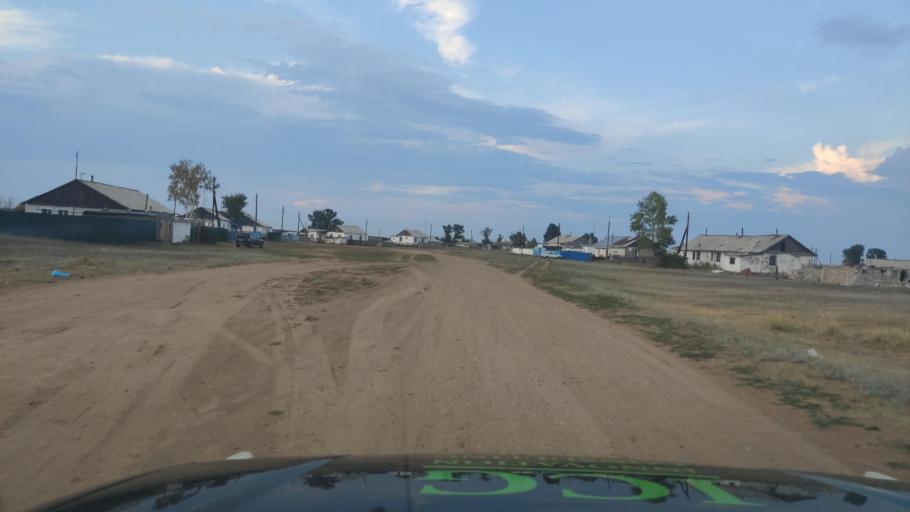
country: KZ
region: Pavlodar
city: Pavlodar
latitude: 52.2885
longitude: 77.4410
